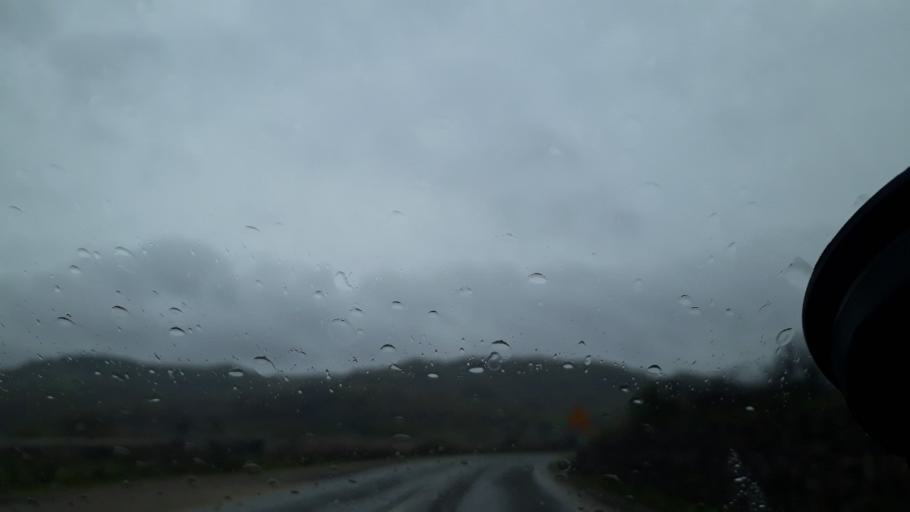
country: BA
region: Republika Srpska
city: Maglajani
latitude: 44.8567
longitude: 17.4559
